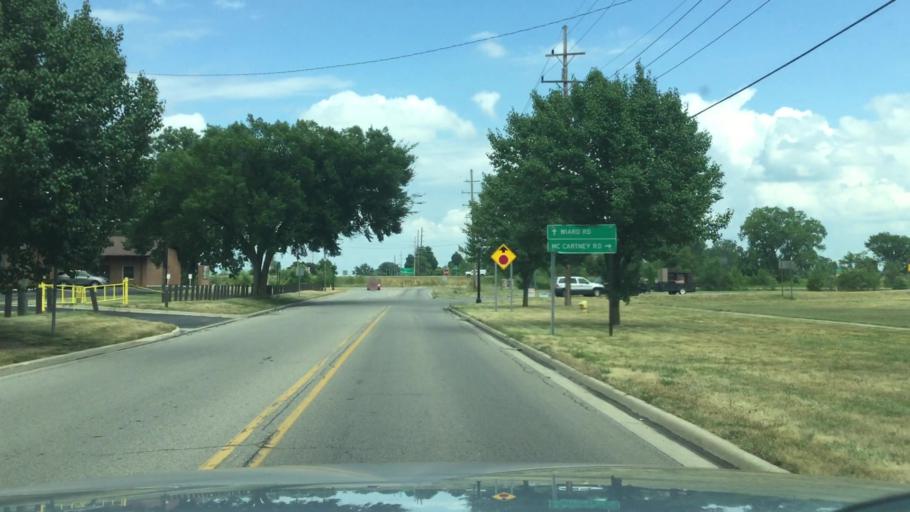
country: US
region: Michigan
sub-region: Washtenaw County
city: Ypsilanti
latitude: 42.2318
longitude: -83.5650
